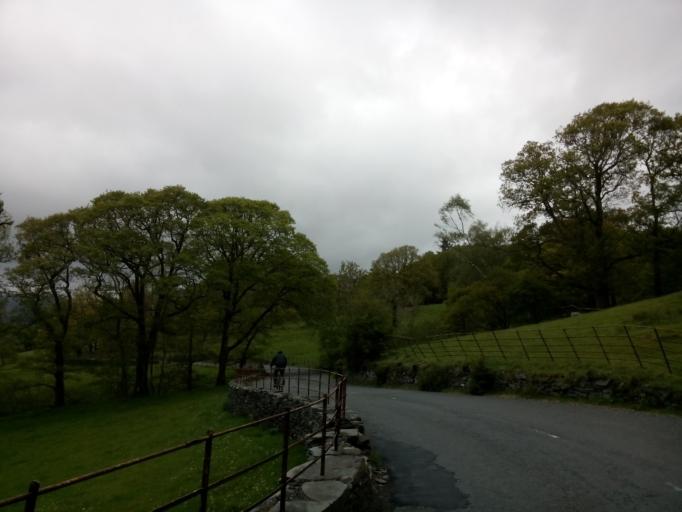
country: GB
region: England
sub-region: Cumbria
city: Ambleside
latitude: 54.4307
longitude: -3.0226
